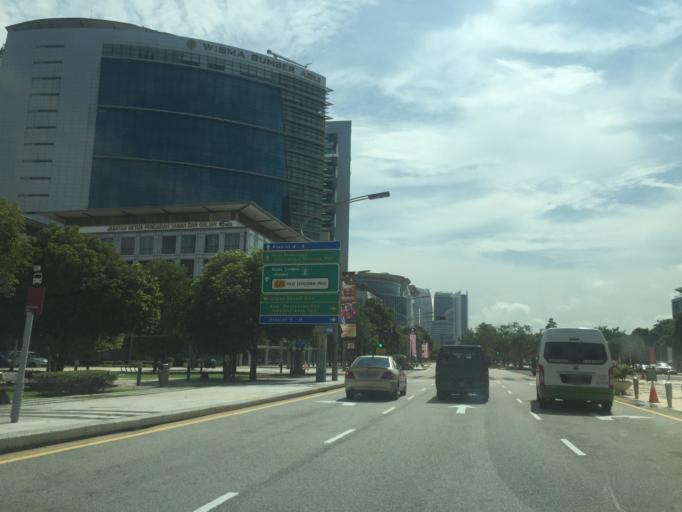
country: MY
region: Putrajaya
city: Putrajaya
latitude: 2.9160
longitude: 101.6847
